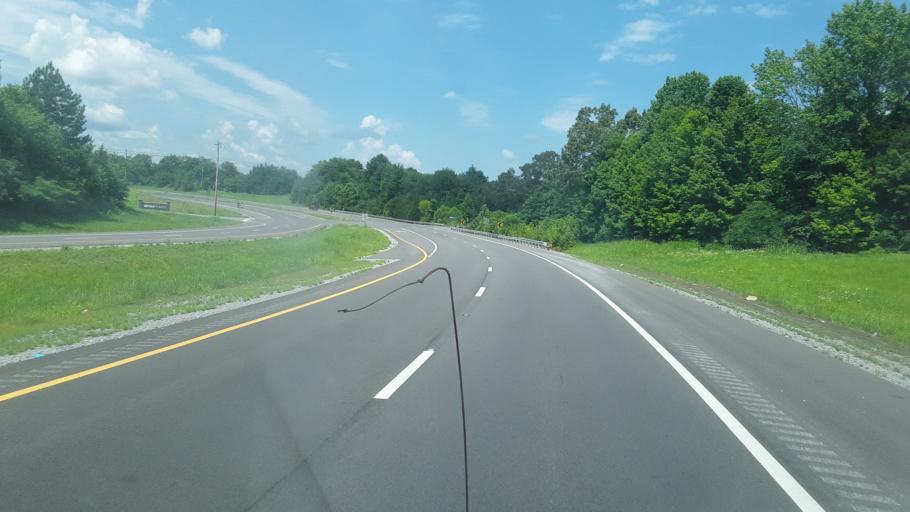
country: US
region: Kentucky
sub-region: Christian County
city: Fort Campbell North
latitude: 36.5824
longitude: -87.4404
